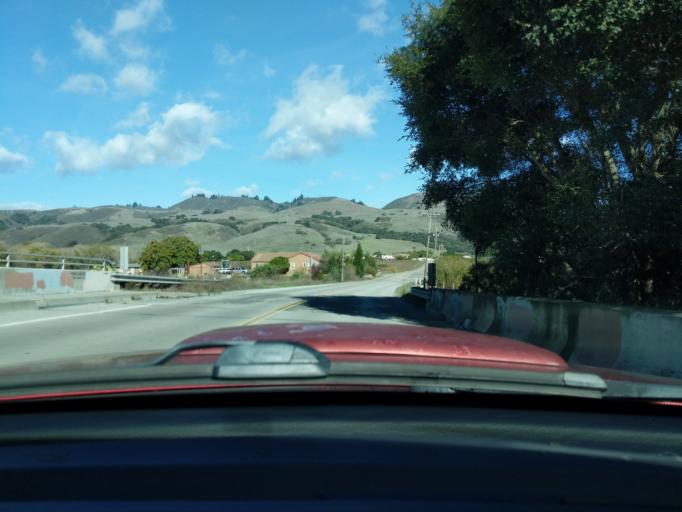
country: US
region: California
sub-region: San Benito County
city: Aromas
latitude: 36.8947
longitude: -121.6440
